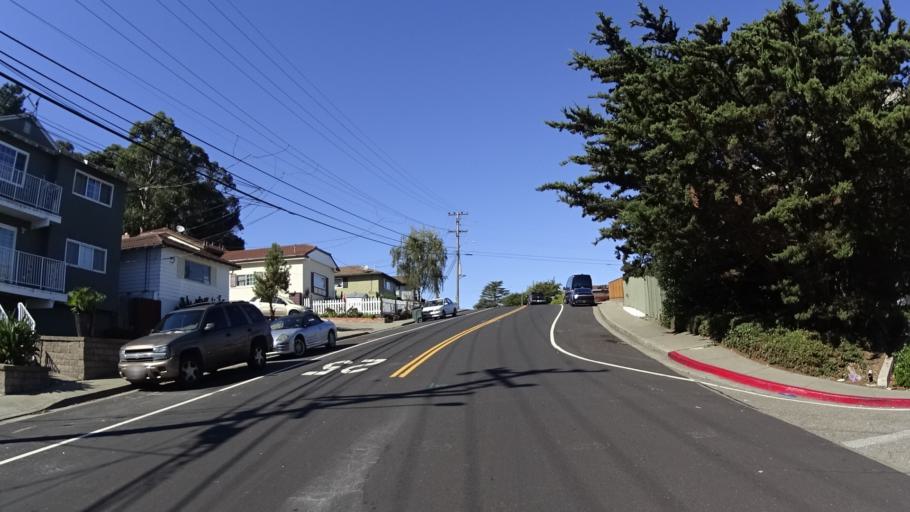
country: US
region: California
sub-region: San Mateo County
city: San Bruno
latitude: 37.6074
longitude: -122.4302
